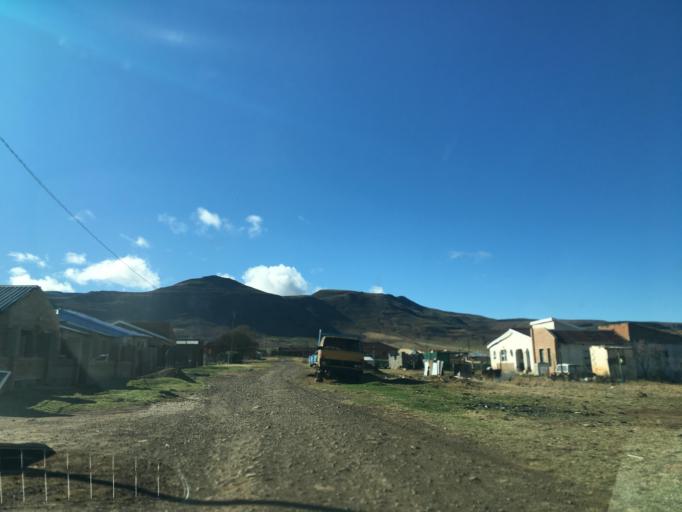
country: ZA
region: Eastern Cape
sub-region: Chris Hani District Municipality
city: Cala
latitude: -31.5380
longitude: 27.6920
